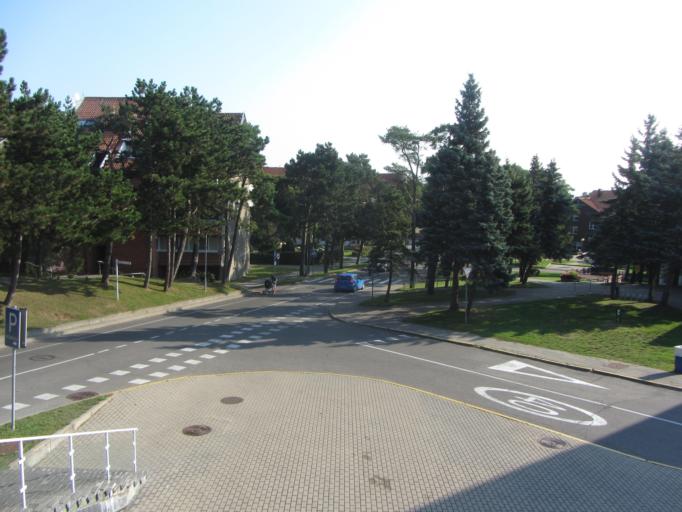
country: LT
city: Nida
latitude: 55.3027
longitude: 21.0018
